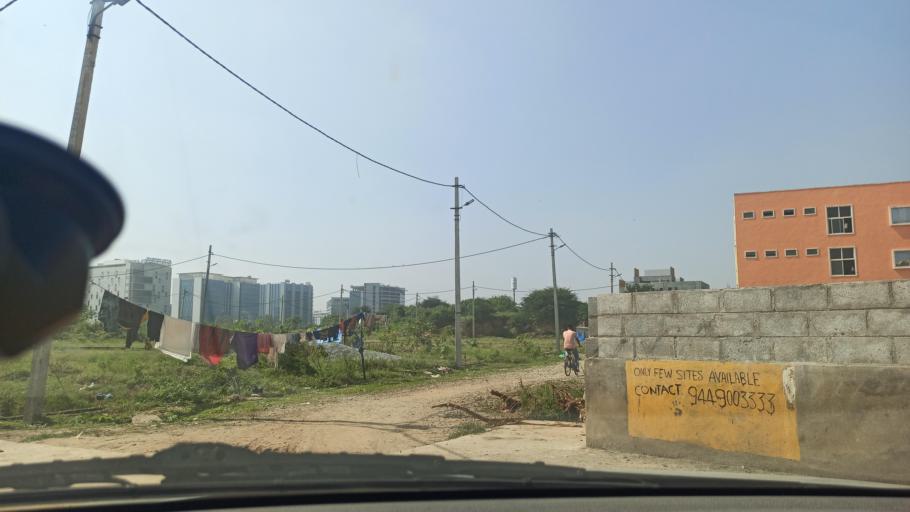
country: IN
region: Karnataka
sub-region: Bangalore Urban
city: Bangalore
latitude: 12.9464
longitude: 77.7018
